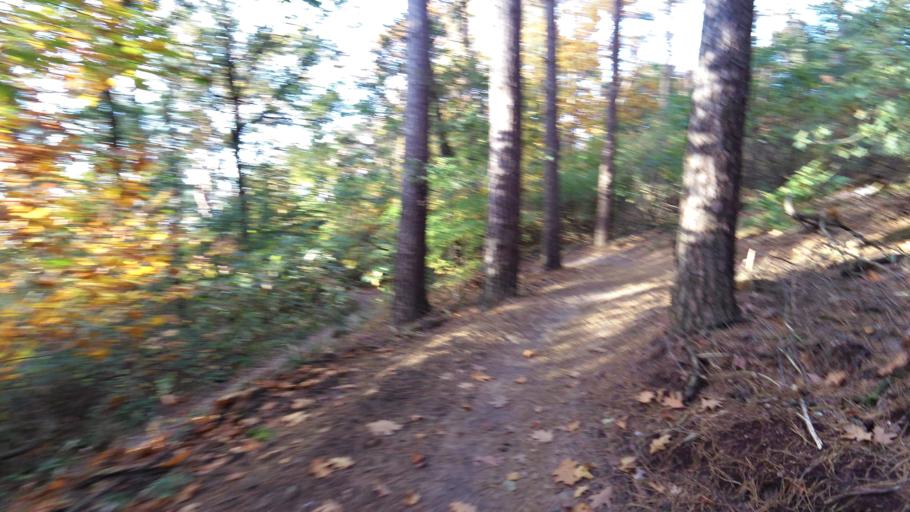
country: NL
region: Gelderland
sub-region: Gemeente Ede
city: Ede
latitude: 52.0668
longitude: 5.6633
